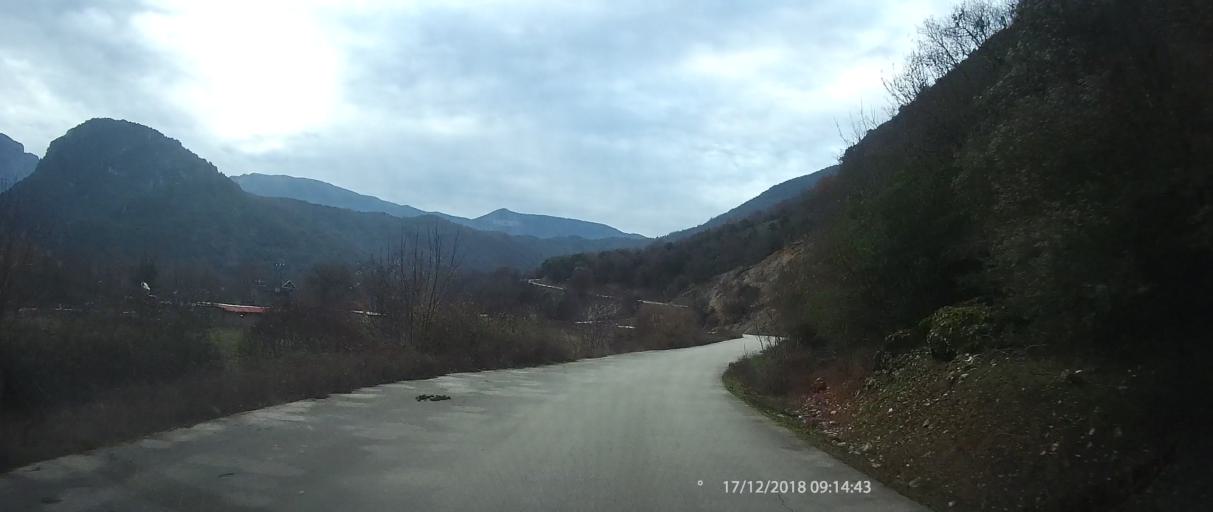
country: GR
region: Epirus
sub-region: Nomos Ioanninon
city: Kalpaki
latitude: 39.9708
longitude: 20.6546
